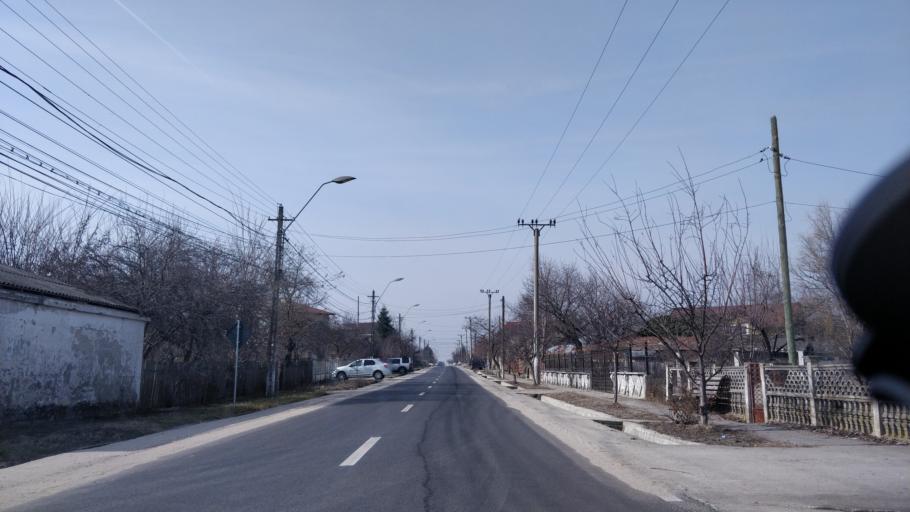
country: RO
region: Giurgiu
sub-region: Comuna Bolintin Deal
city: Bolintin Deal
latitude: 44.4610
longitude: 25.8088
